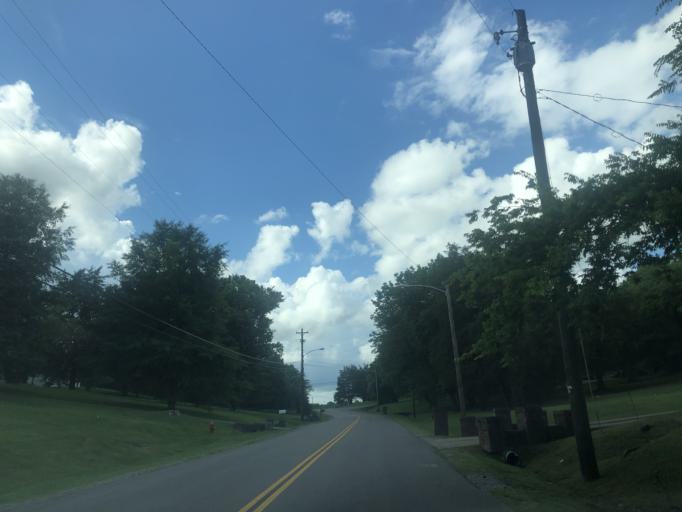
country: US
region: Tennessee
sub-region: Davidson County
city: Nashville
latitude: 36.2139
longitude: -86.8553
